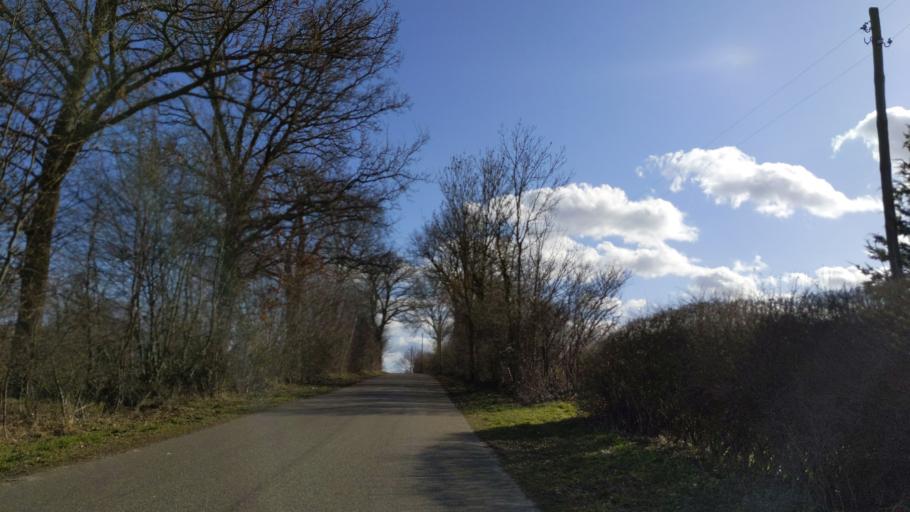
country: DE
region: Schleswig-Holstein
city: Travemuende
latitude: 53.9545
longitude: 10.8412
